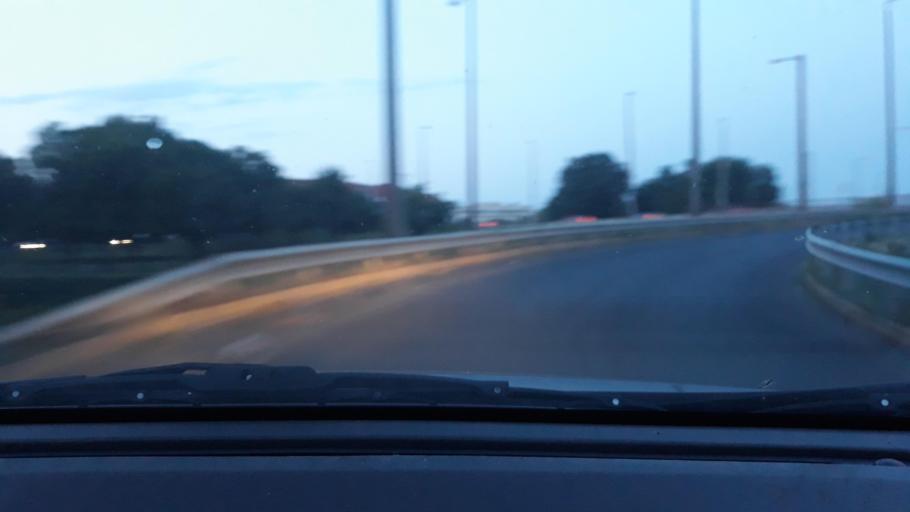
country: HU
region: Hajdu-Bihar
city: Debrecen
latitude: 47.5226
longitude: 21.6315
